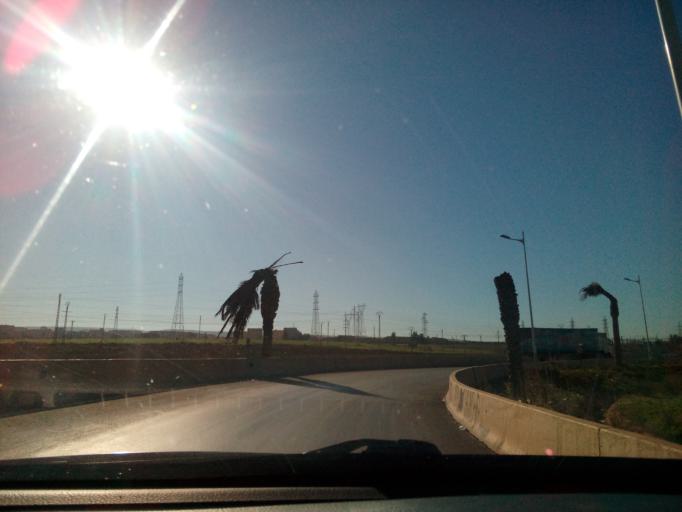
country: DZ
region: Chlef
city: Oued Sly
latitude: 36.0924
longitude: 1.2019
